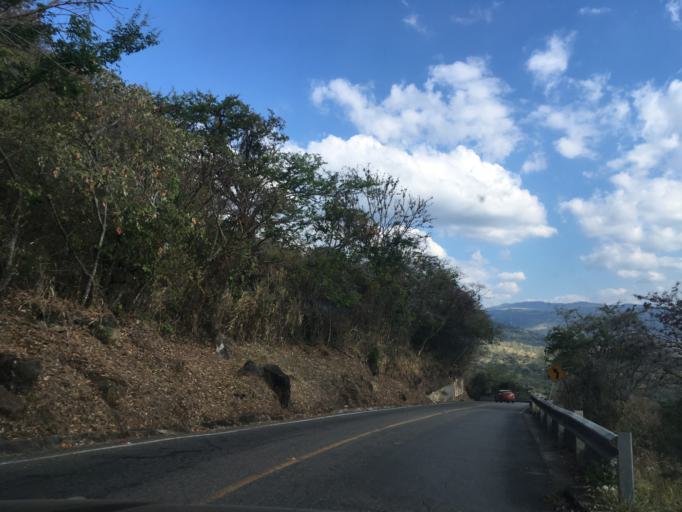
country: CO
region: Santander
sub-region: San Gil
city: San Gil
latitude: 6.5719
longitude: -73.1424
